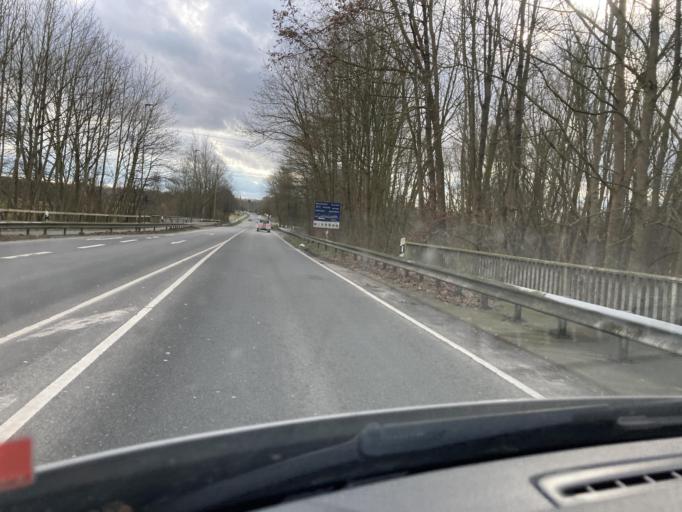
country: DE
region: Lower Saxony
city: Fedderwarden
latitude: 53.5579
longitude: 8.0805
